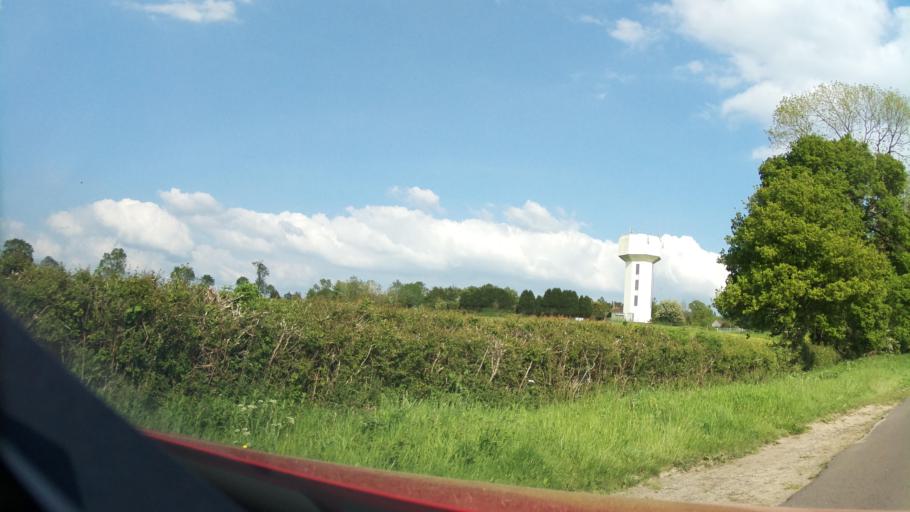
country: GB
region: England
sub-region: Wiltshire
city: Malmesbury
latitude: 51.5496
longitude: -2.1027
